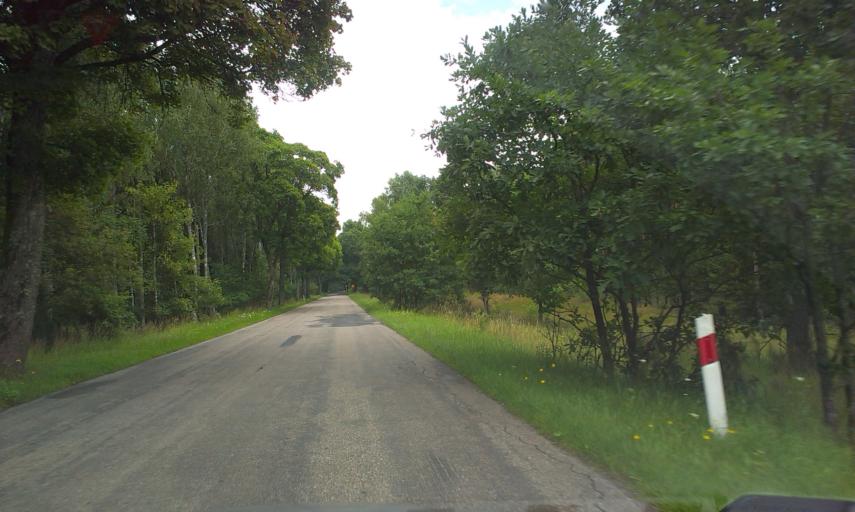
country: PL
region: West Pomeranian Voivodeship
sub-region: Powiat szczecinecki
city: Barwice
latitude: 53.6673
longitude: 16.3393
